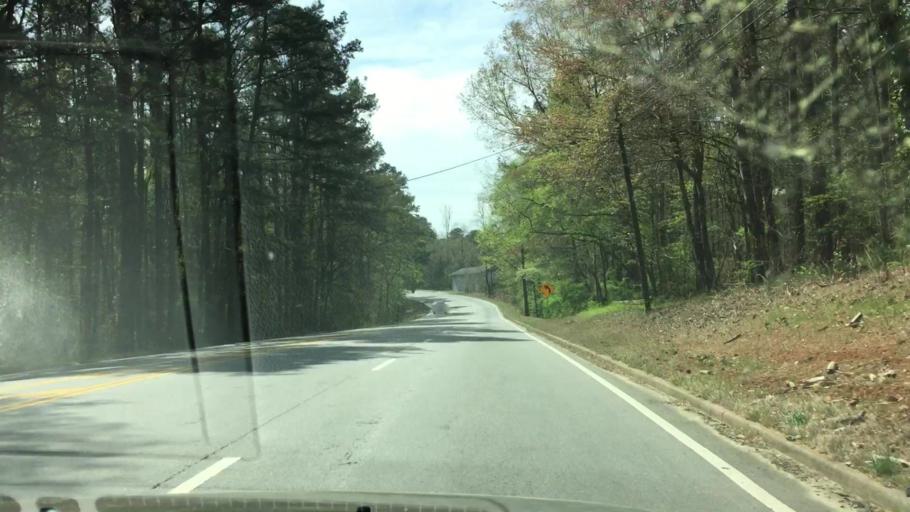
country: US
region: Georgia
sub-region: Barrow County
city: Winder
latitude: 34.0226
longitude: -83.7106
